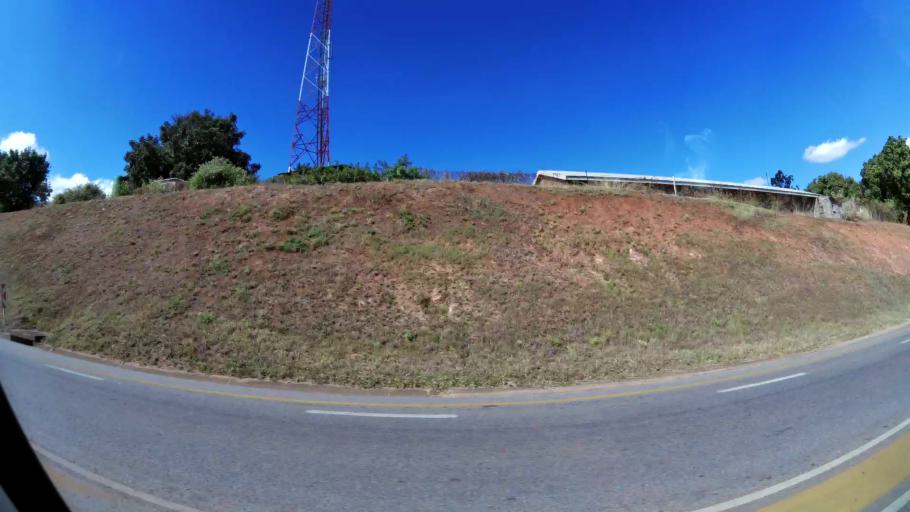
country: ZA
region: Limpopo
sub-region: Mopani District Municipality
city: Tzaneen
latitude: -23.8164
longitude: 30.1707
